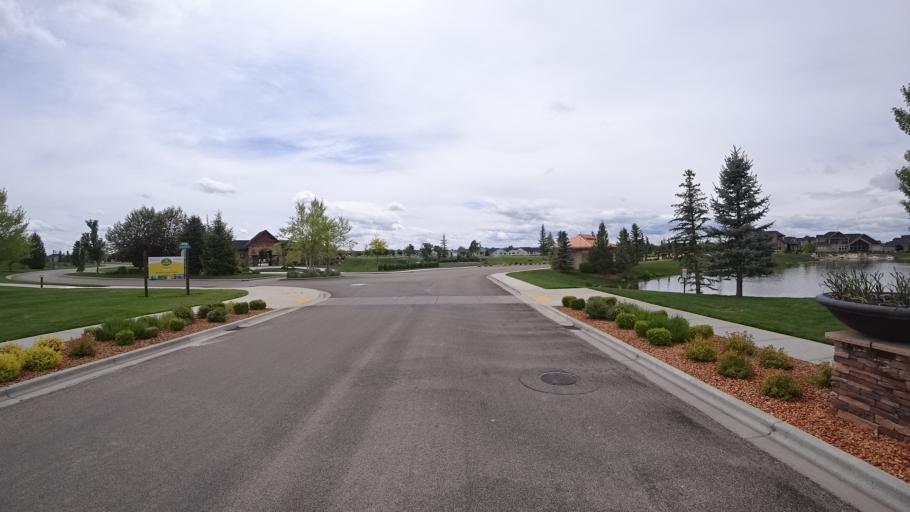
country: US
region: Idaho
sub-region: Ada County
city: Star
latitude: 43.7052
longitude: -116.4269
